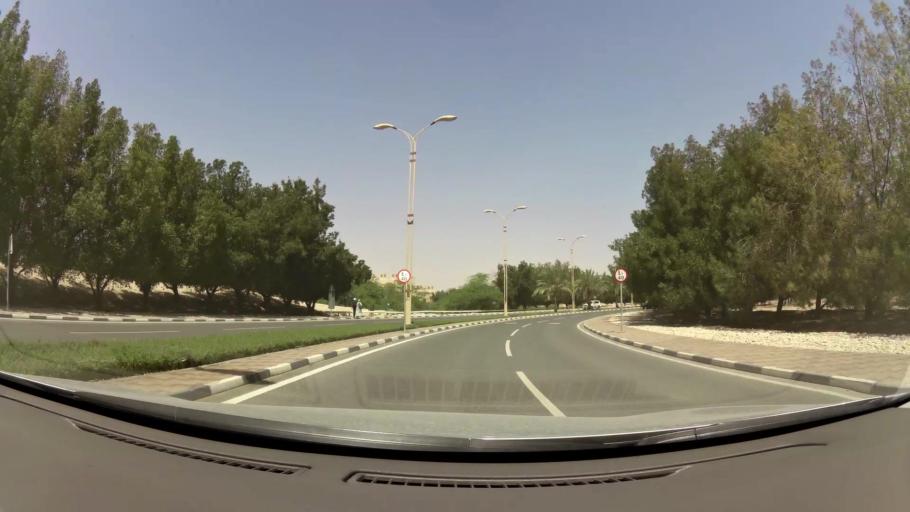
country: QA
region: Baladiyat ad Dawhah
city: Doha
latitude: 25.3700
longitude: 51.4936
